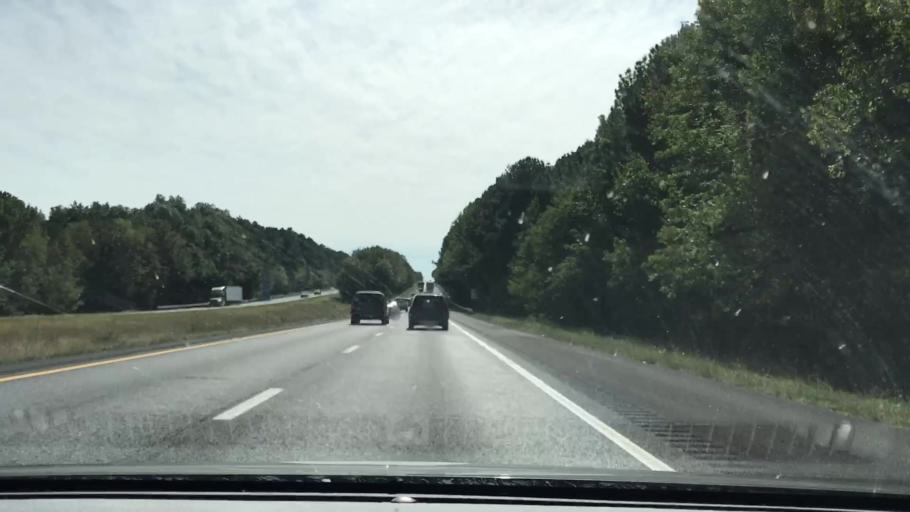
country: US
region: Tennessee
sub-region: Robertson County
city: Cross Plains
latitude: 36.5648
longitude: -86.6228
